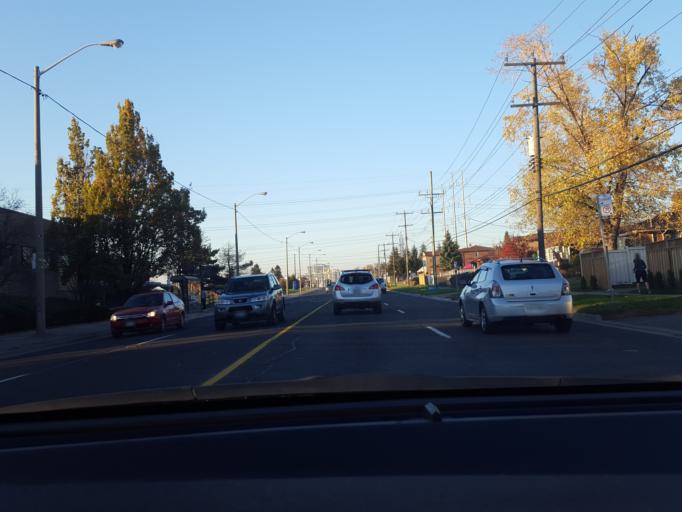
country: CA
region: Ontario
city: Scarborough
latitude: 43.7366
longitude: -79.2804
